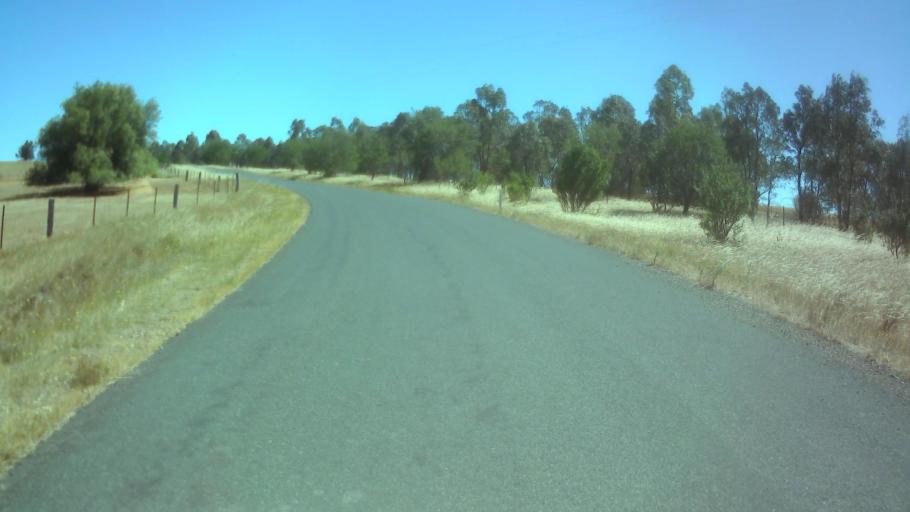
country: AU
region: New South Wales
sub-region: Weddin
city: Grenfell
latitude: -33.9647
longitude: 148.4065
